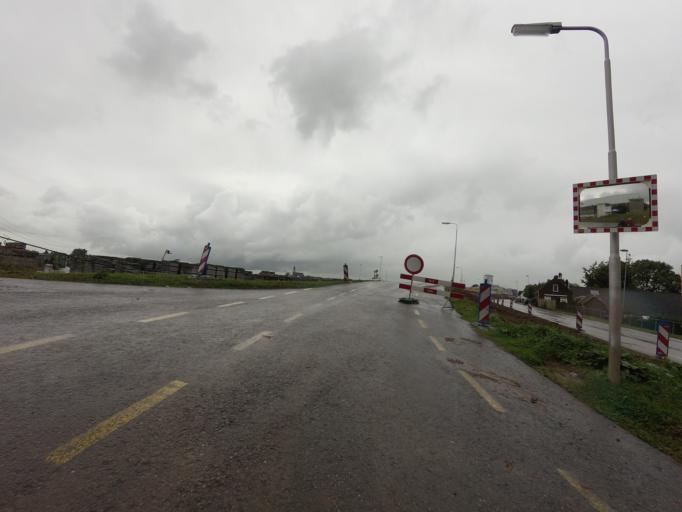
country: NL
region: South Holland
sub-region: Molenwaard
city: Nieuw-Lekkerland
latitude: 51.8898
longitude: 4.6806
